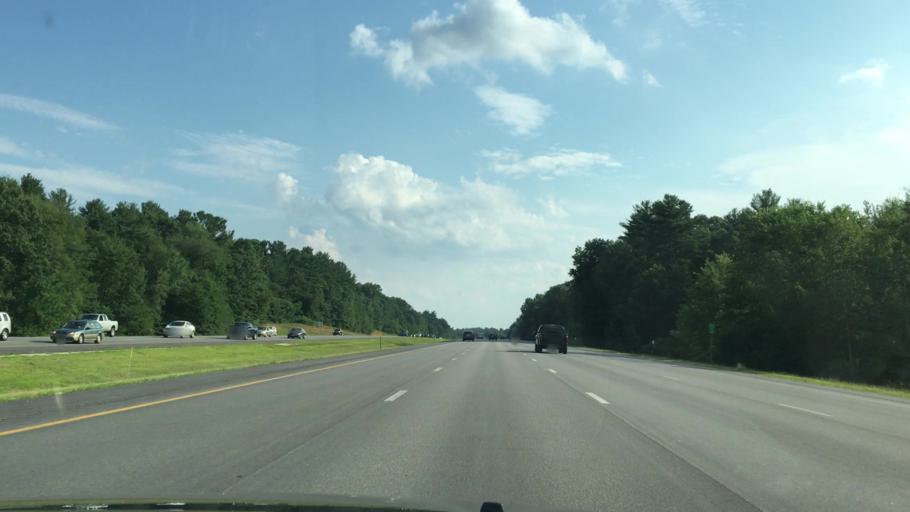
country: US
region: New Hampshire
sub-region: Rockingham County
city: Hampton Falls
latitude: 42.9181
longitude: -70.8711
